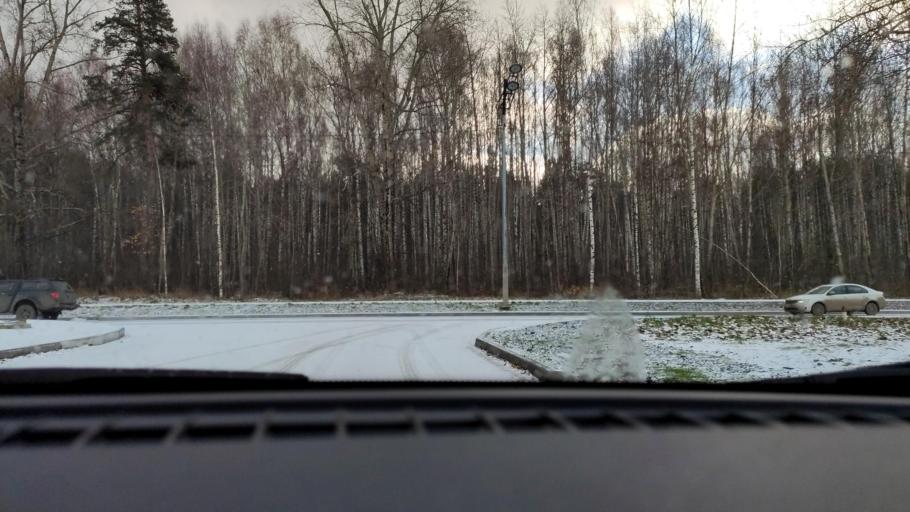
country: RU
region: Perm
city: Kondratovo
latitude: 57.9958
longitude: 56.1634
